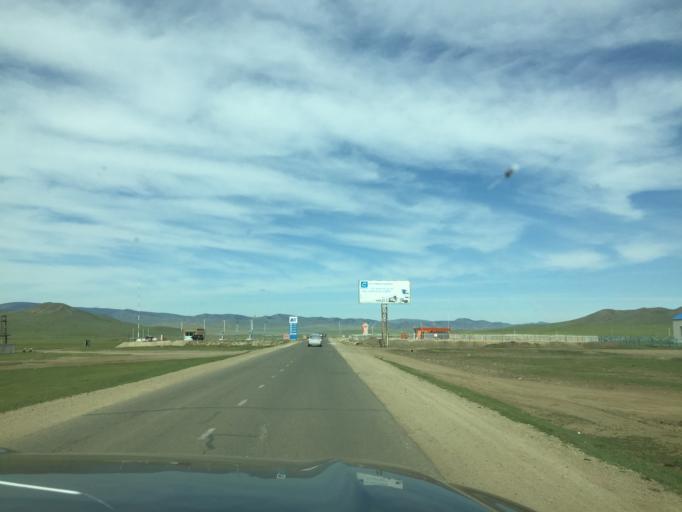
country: MN
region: Central Aimak
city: Ihsueuej
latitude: 48.2280
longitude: 106.2870
